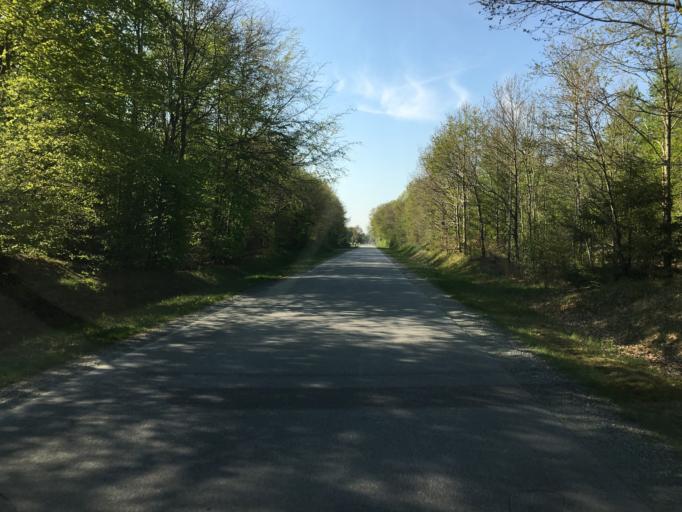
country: DK
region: South Denmark
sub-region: Haderslev Kommune
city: Vojens
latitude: 55.2423
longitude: 9.3198
